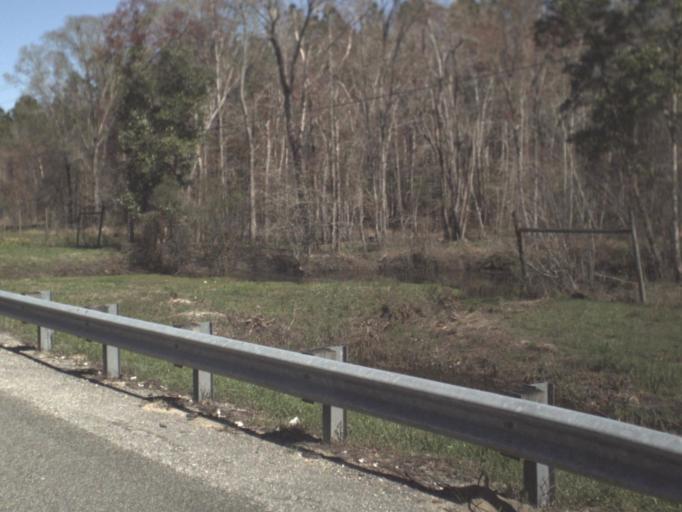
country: US
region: Florida
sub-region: Jackson County
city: Sneads
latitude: 30.5987
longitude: -85.0294
